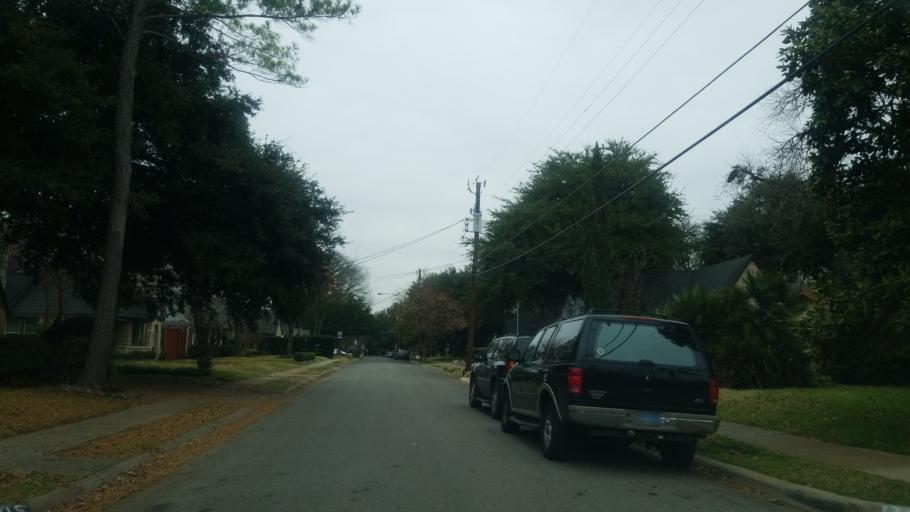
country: US
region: Texas
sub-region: Dallas County
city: Highland Park
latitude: 32.8211
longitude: -96.8265
